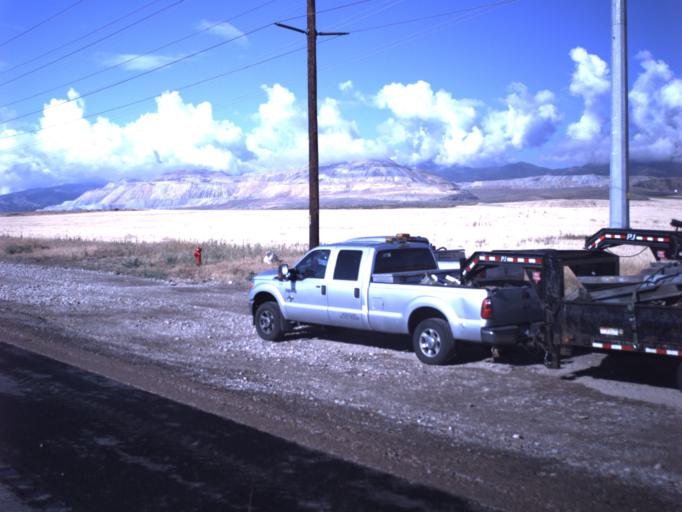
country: US
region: Utah
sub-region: Salt Lake County
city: Oquirrh
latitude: 40.5916
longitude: -112.0588
